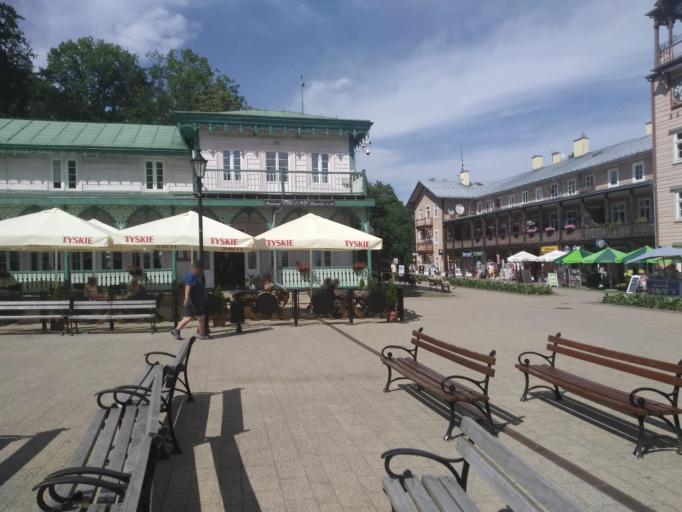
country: PL
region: Subcarpathian Voivodeship
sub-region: Powiat krosnienski
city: Iwonicz-Zdroj
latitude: 49.5621
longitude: 21.7884
